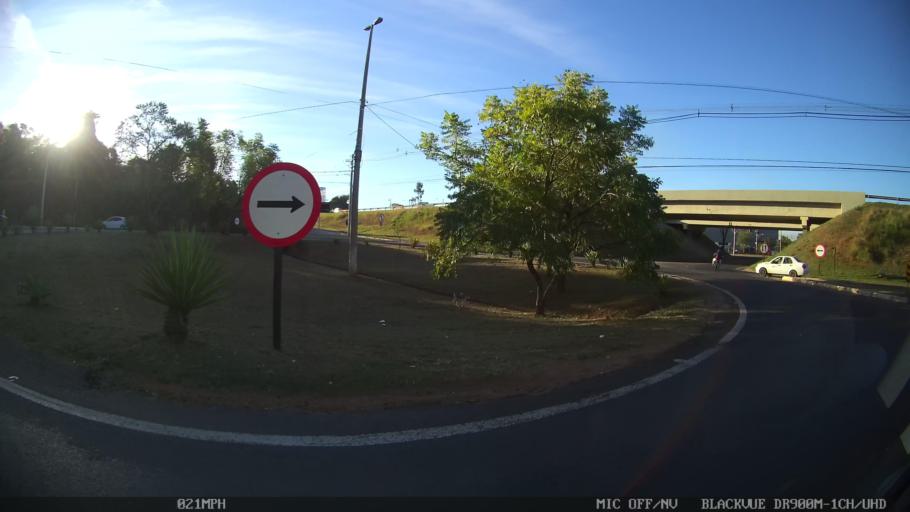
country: BR
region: Sao Paulo
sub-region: Sao Jose Do Rio Preto
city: Sao Jose do Rio Preto
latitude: -20.8714
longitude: -49.3261
